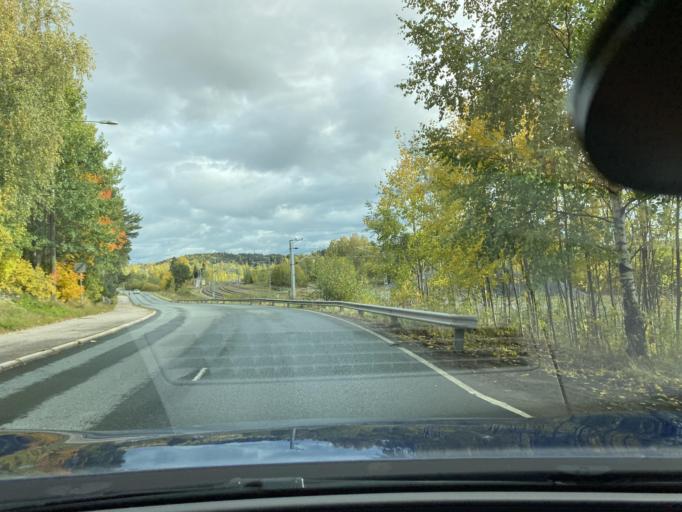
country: FI
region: Pirkanmaa
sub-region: Tampere
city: Nokia
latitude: 61.4751
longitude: 23.3445
